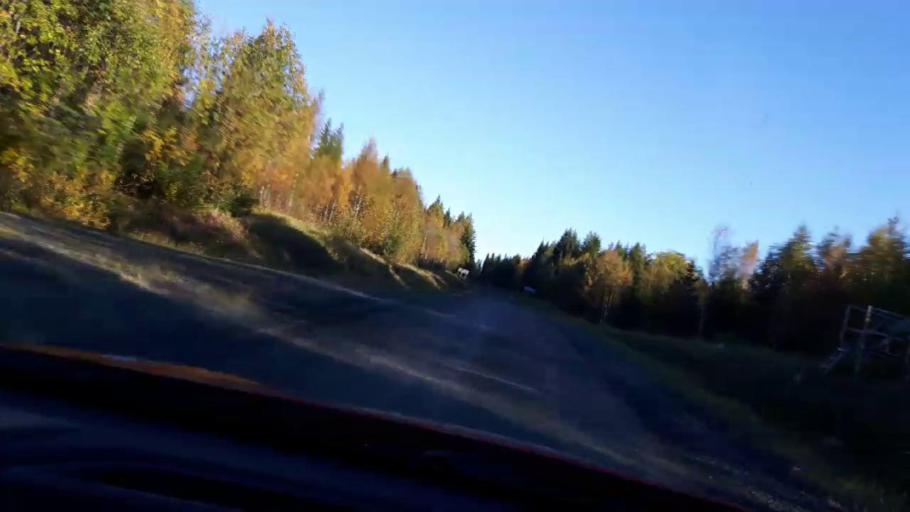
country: SE
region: Jaemtland
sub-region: OEstersunds Kommun
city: Lit
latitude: 63.5734
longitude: 14.8694
